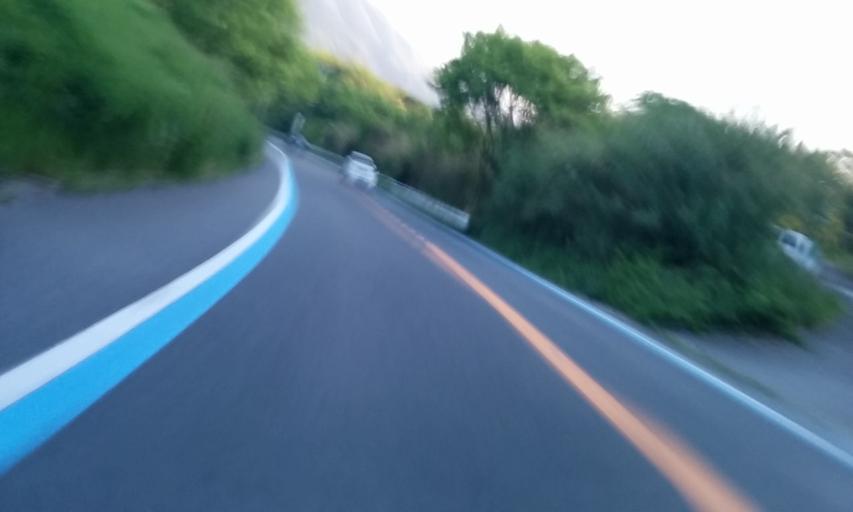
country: JP
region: Ehime
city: Iyo
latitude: 33.7138
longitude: 132.6678
